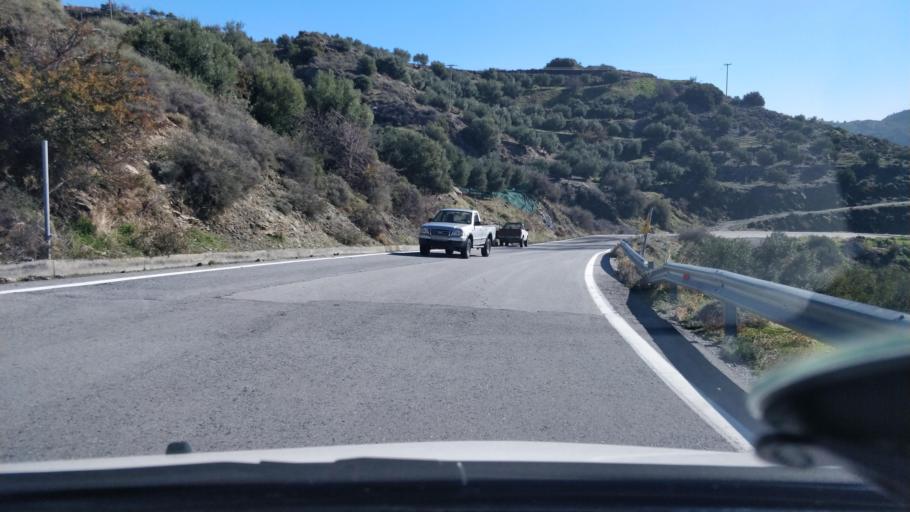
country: GR
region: Crete
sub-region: Nomos Irakleiou
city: Kastelli
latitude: 35.0360
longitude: 25.4428
